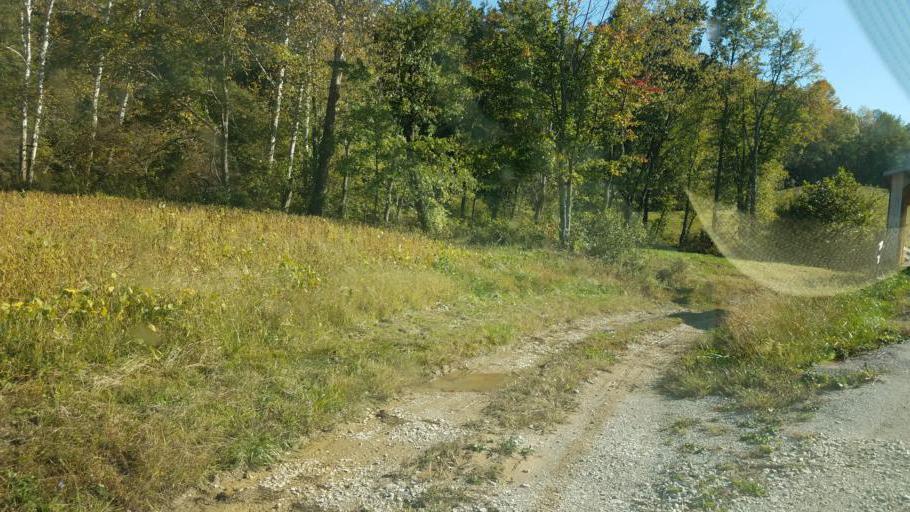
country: US
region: Kentucky
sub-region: Fleming County
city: Flemingsburg
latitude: 38.4633
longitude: -83.5608
